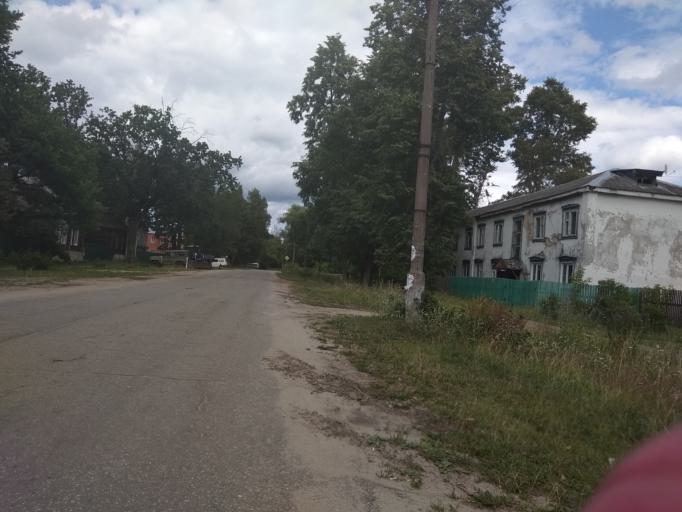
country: RU
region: Moskovskaya
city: Misheronskiy
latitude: 55.7196
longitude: 39.7397
